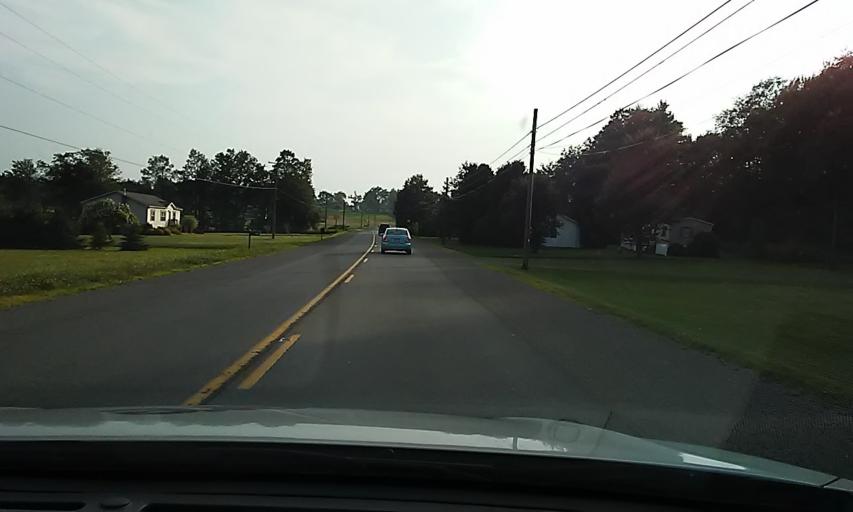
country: US
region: Pennsylvania
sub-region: McKean County
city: Kane
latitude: 41.7012
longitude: -78.7058
